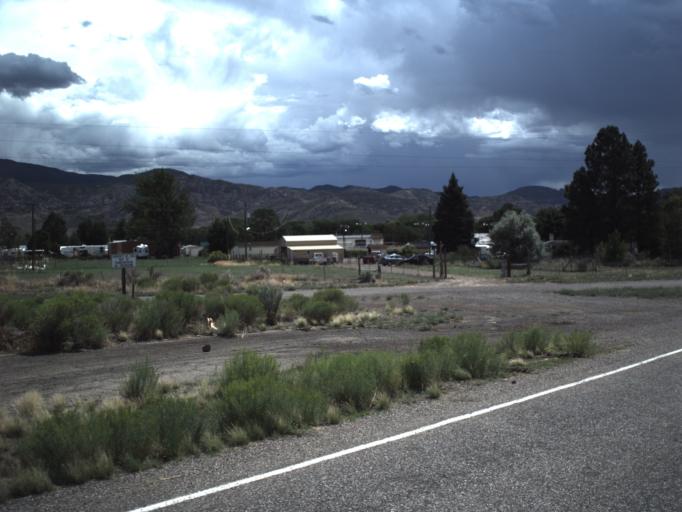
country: US
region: Utah
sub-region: Piute County
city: Junction
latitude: 38.2392
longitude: -112.2282
